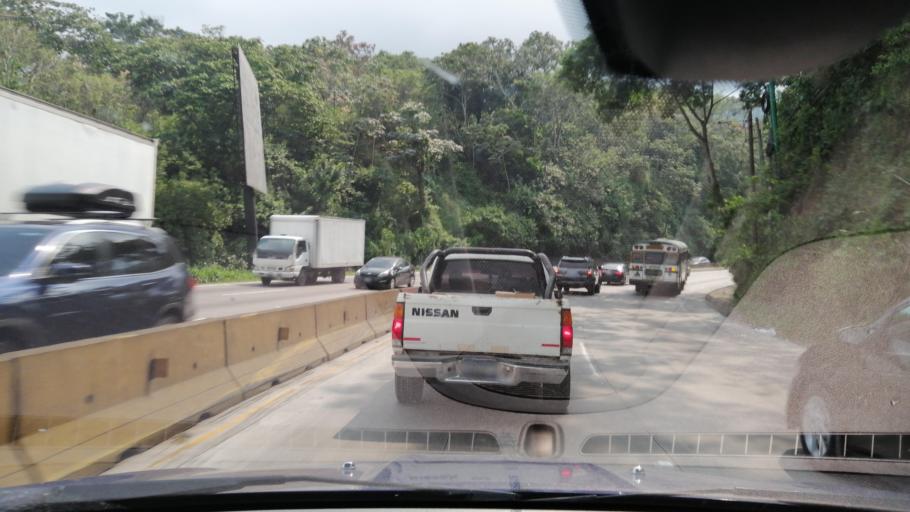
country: SV
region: La Libertad
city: Santa Tecla
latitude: 13.6766
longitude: -89.3086
